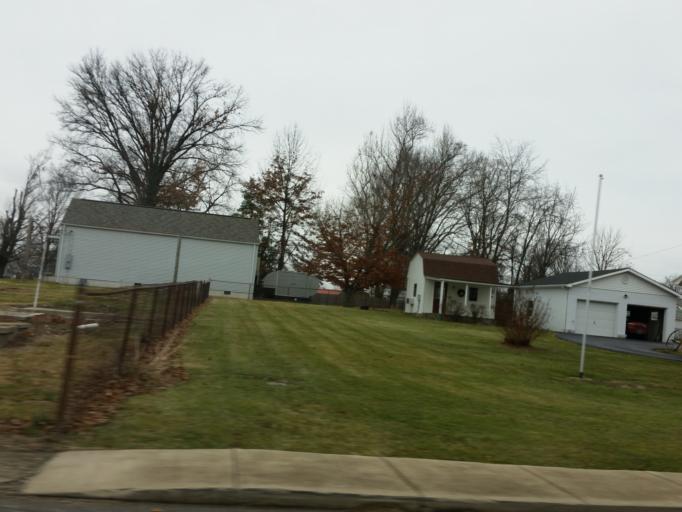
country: US
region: Kentucky
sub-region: Trimble County
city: Providence
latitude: 38.5238
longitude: -85.2038
